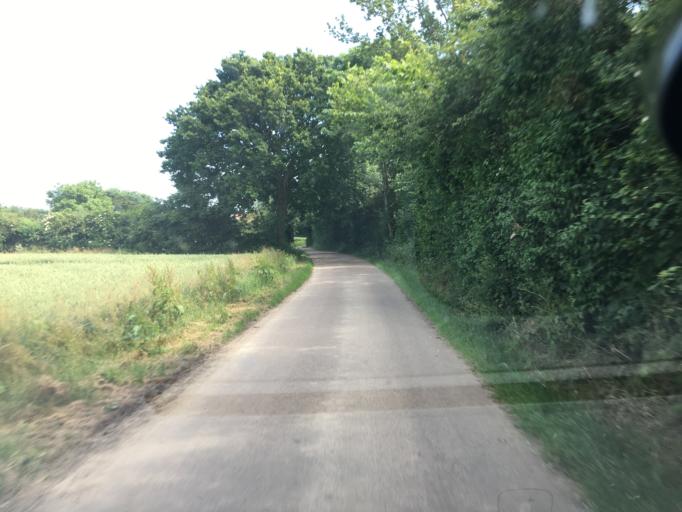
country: DK
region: South Denmark
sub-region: Sonderborg Kommune
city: Dybbol
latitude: 54.9560
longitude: 9.7383
